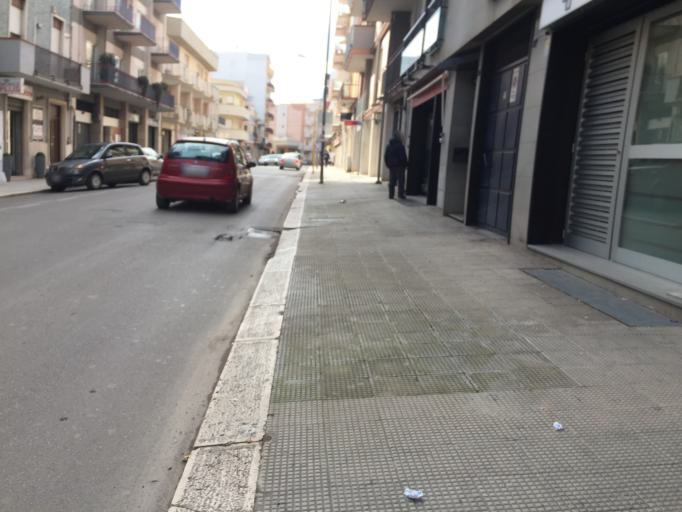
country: IT
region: Apulia
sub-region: Provincia di Barletta - Andria - Trani
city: Andria
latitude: 41.2247
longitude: 16.3052
